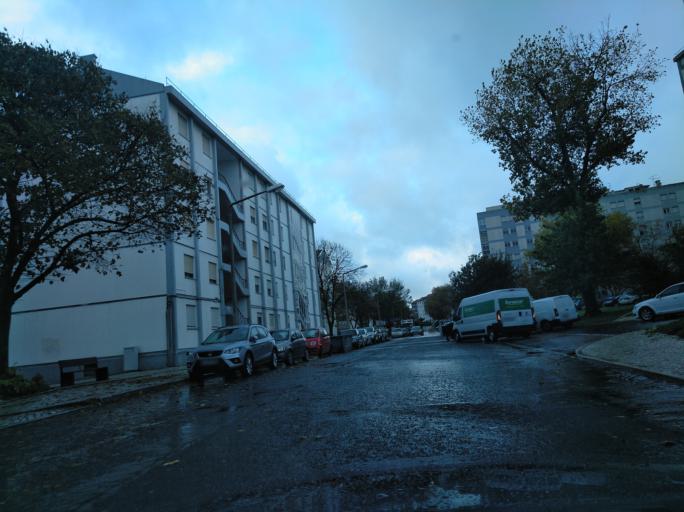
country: PT
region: Lisbon
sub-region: Loures
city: Moscavide
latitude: 38.7580
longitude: -9.1068
